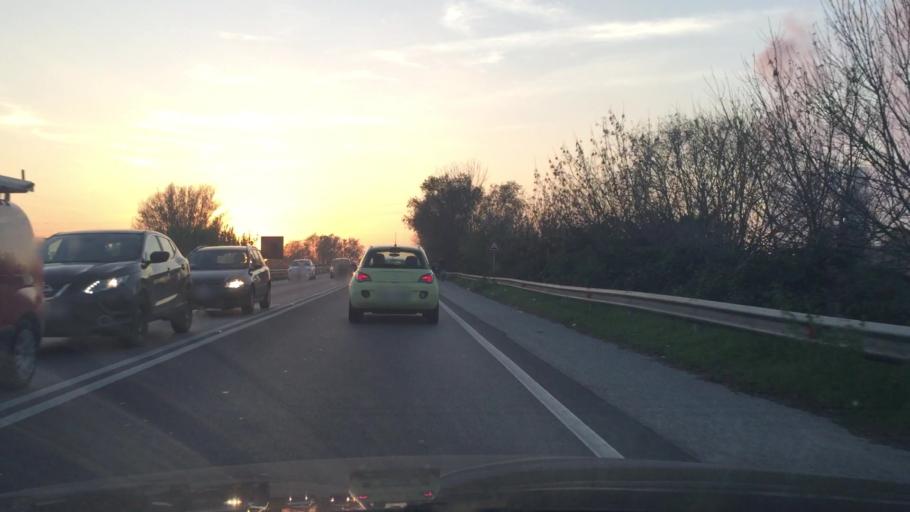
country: IT
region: Emilia-Romagna
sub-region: Provincia di Ferrara
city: Ferrara
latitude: 44.8543
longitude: 11.5995
